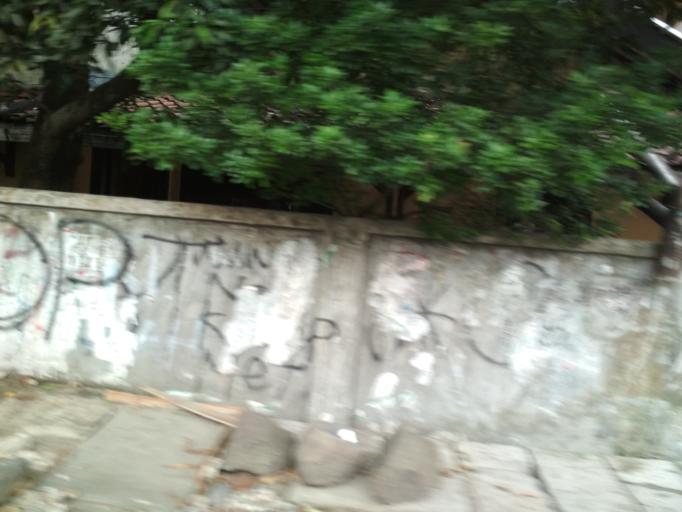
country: ID
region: West Java
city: Bogor
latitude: -6.5933
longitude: 106.7770
